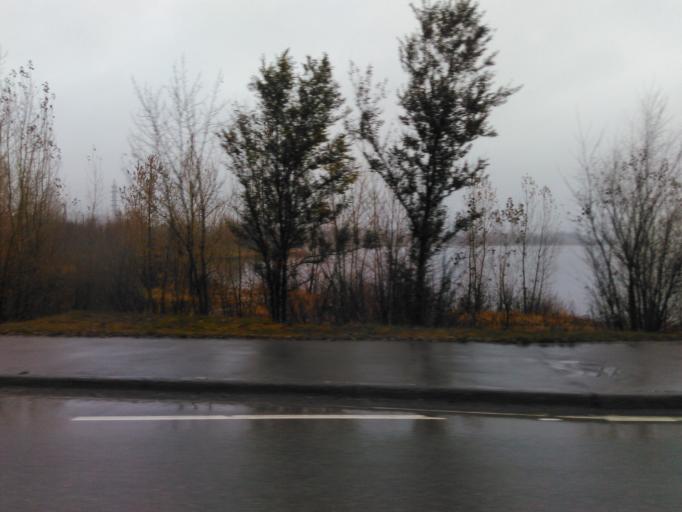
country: RU
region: Tatarstan
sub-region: Gorod Kazan'
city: Kazan
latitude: 55.8002
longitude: 49.0716
